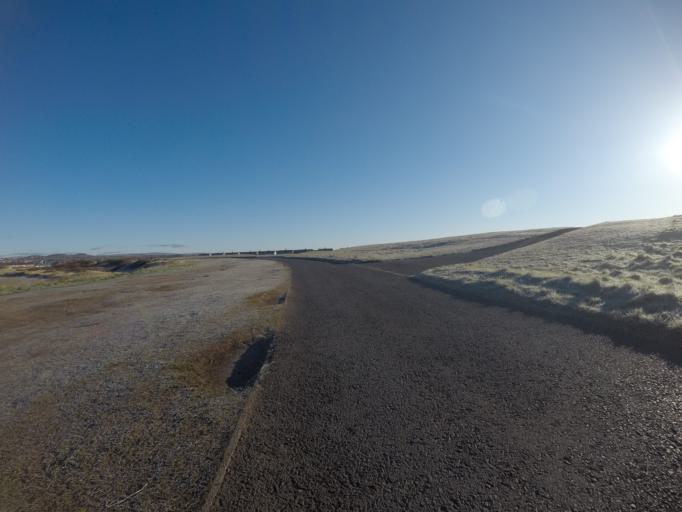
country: GB
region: Scotland
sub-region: North Ayrshire
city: Stevenston
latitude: 55.6271
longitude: -4.7485
